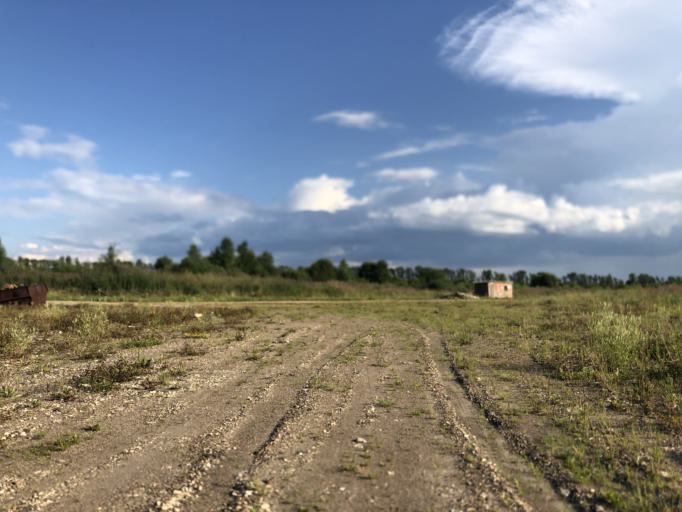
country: RU
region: Tverskaya
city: Rzhev
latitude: 56.2679
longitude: 34.2421
